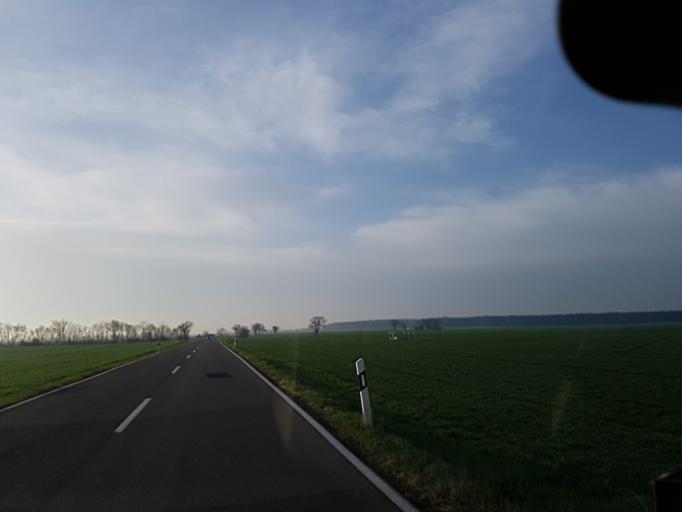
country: DE
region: Saxony
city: Strehla
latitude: 51.3959
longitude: 13.2681
